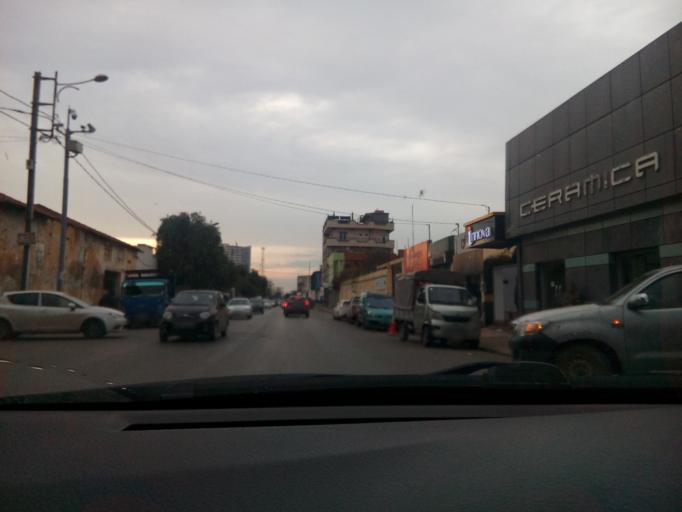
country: DZ
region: Oran
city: Oran
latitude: 35.6860
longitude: -0.6406
